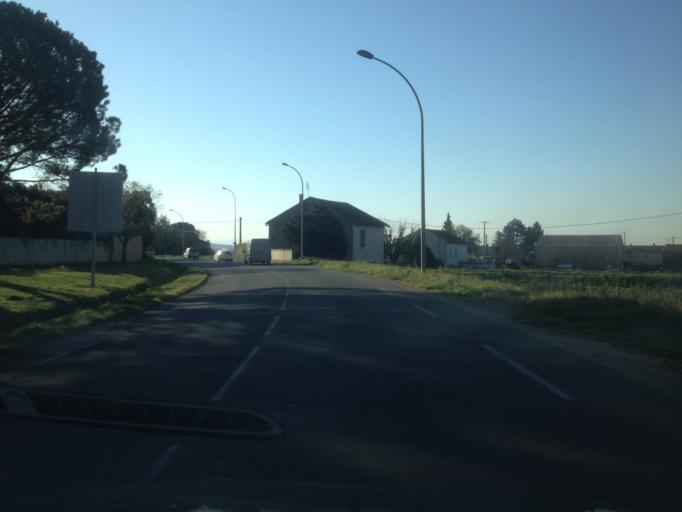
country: FR
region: Provence-Alpes-Cote d'Azur
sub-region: Departement du Vaucluse
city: Chateauneuf-du-Pape
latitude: 44.0498
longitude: 4.8360
